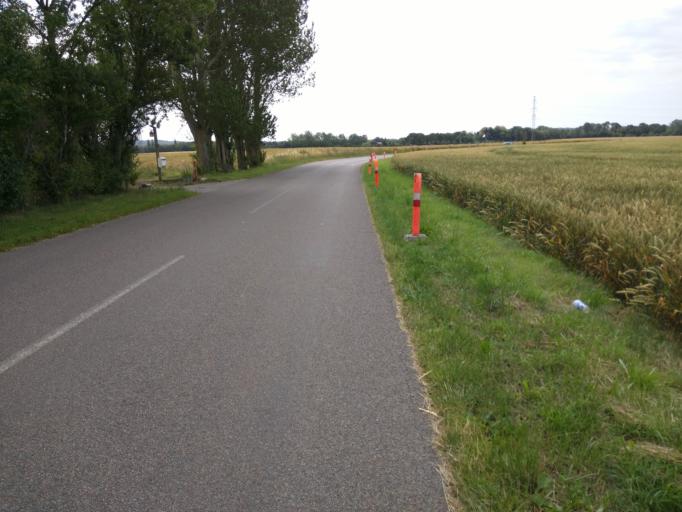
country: DK
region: Zealand
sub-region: Kalundborg Kommune
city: Svebolle
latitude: 55.6935
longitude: 11.3069
